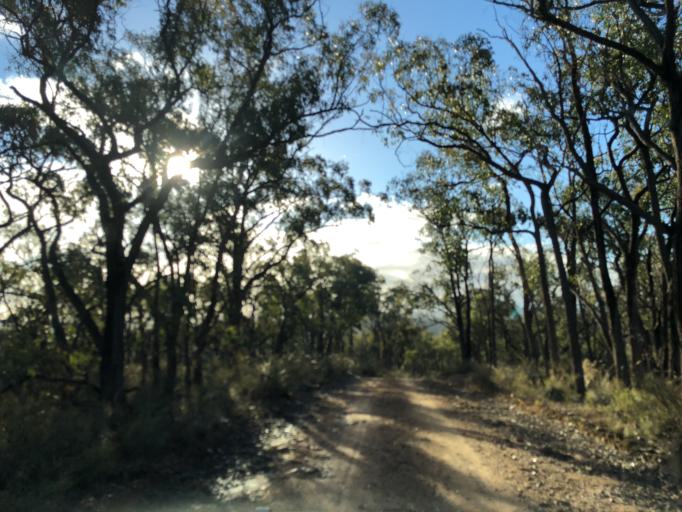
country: AU
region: Victoria
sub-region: Mount Alexander
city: Castlemaine
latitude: -37.2306
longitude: 144.2686
